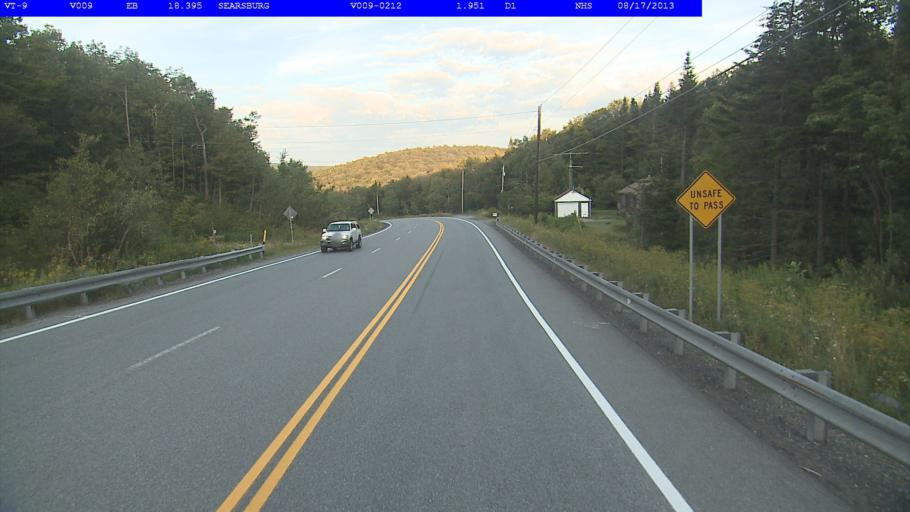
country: US
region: Vermont
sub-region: Windham County
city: Dover
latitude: 42.8949
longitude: -72.9740
